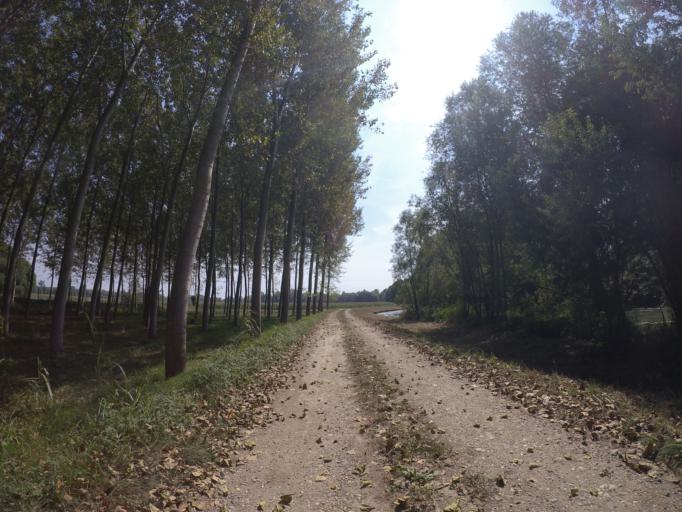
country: IT
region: Friuli Venezia Giulia
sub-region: Provincia di Udine
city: Varmo
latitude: 45.9102
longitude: 13.0190
